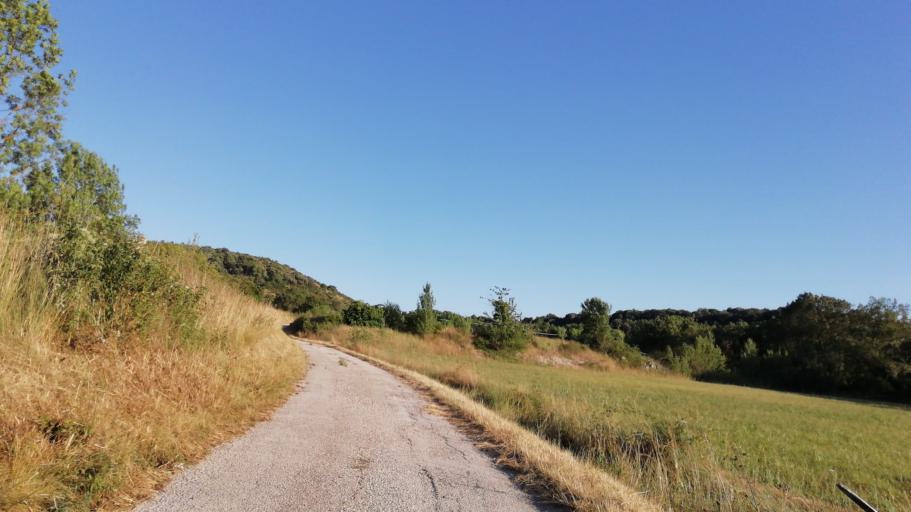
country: FR
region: Languedoc-Roussillon
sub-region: Departement de l'Herault
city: Saint-Martin-de-Londres
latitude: 43.7796
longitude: 3.7275
